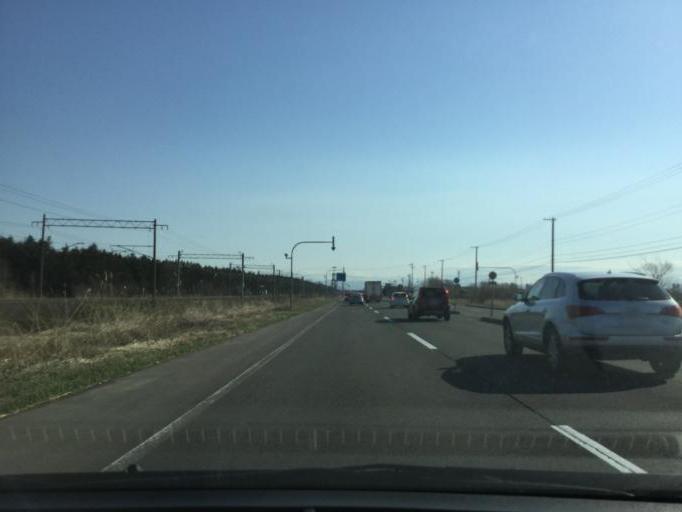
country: JP
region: Hokkaido
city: Iwamizawa
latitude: 43.1702
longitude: 141.6929
